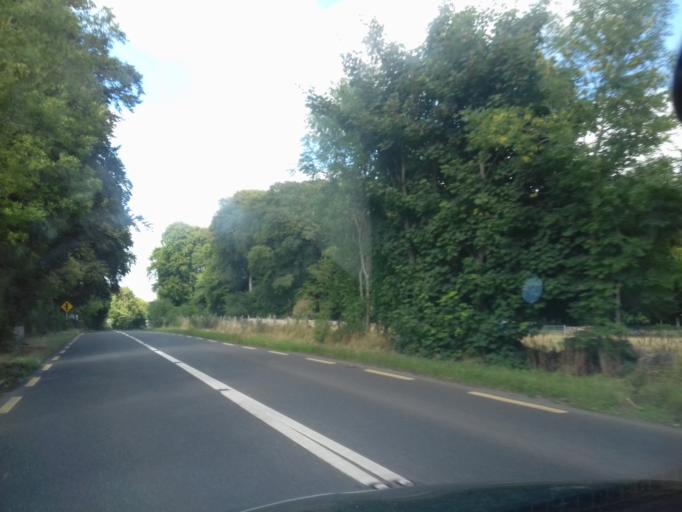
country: IE
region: Leinster
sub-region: Wicklow
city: Valleymount
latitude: 53.1385
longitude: -6.5616
